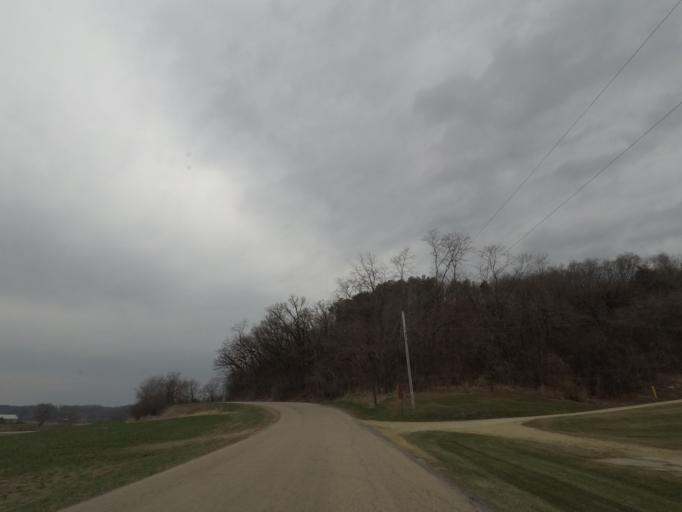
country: US
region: Wisconsin
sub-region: Dane County
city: Cross Plains
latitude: 43.0965
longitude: -89.6070
